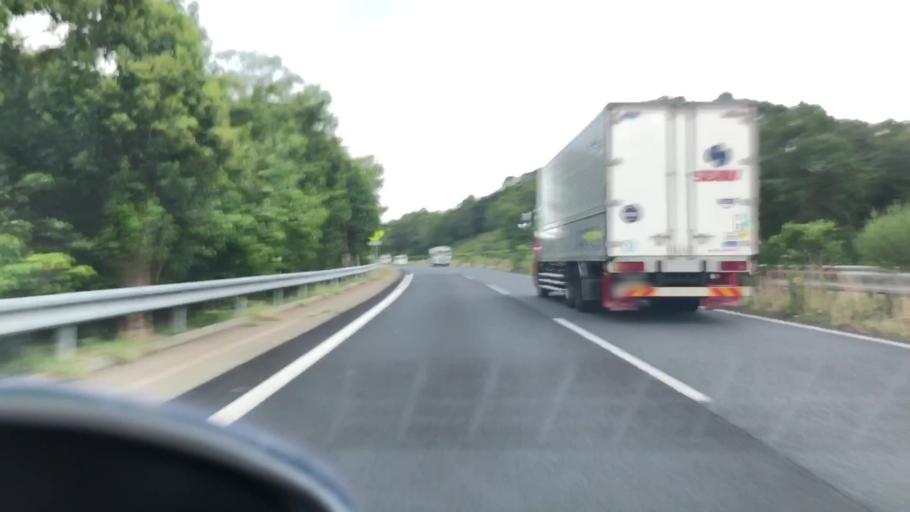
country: JP
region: Hyogo
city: Yashiro
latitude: 34.9153
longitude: 135.0256
